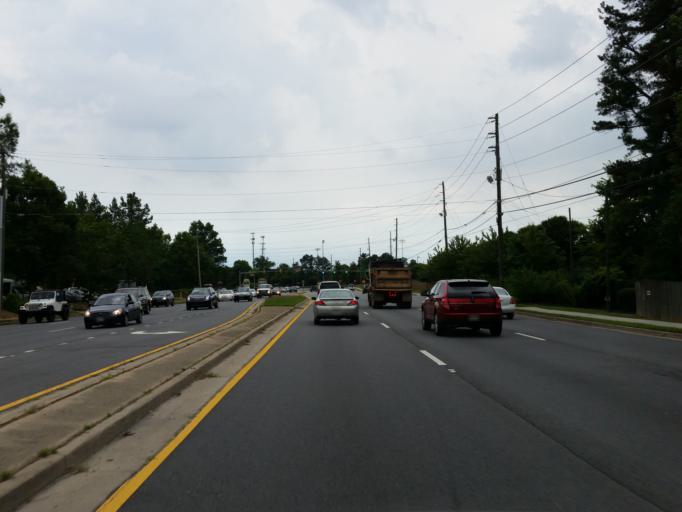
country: US
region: Georgia
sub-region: Fulton County
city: Sandy Springs
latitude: 33.9713
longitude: -84.4134
